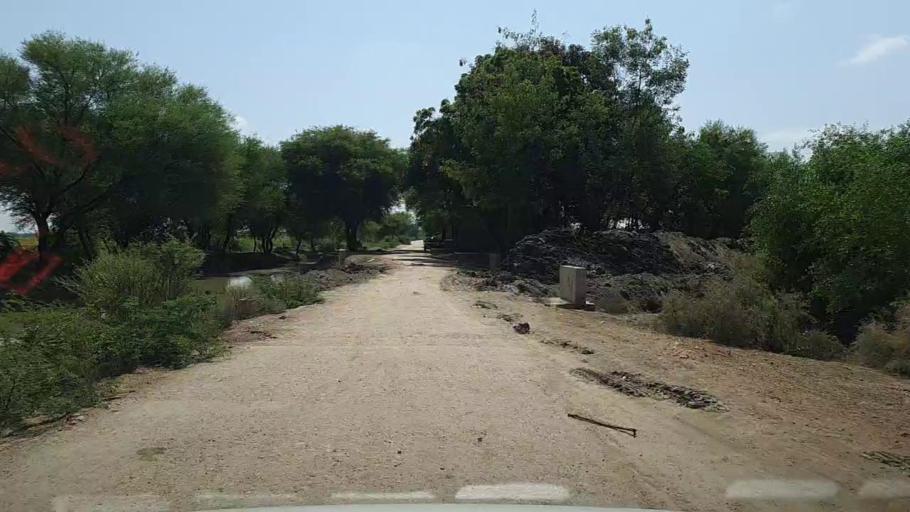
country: PK
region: Sindh
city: Kario
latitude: 24.8777
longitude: 68.6882
